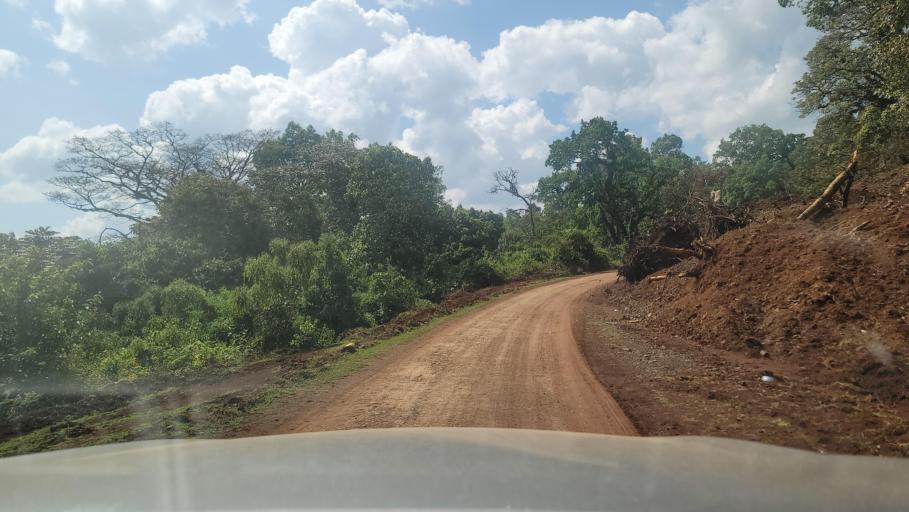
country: ET
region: Oromiya
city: Agaro
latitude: 7.7106
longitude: 36.2542
